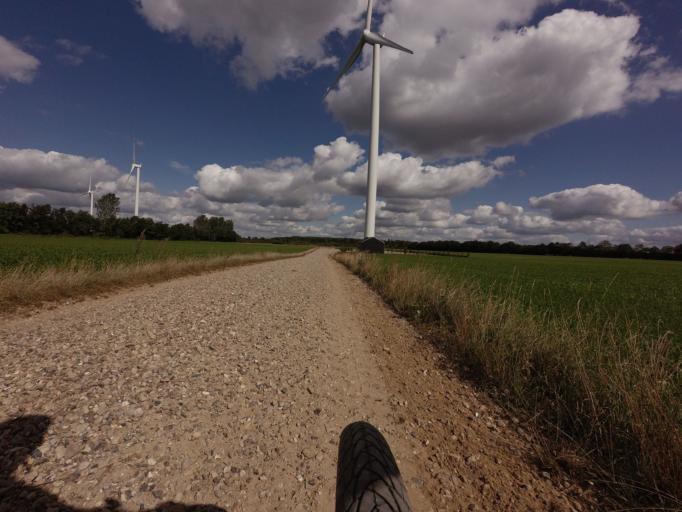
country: DK
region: Central Jutland
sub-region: Ikast-Brande Kommune
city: Brande
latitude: 55.9745
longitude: 9.1251
